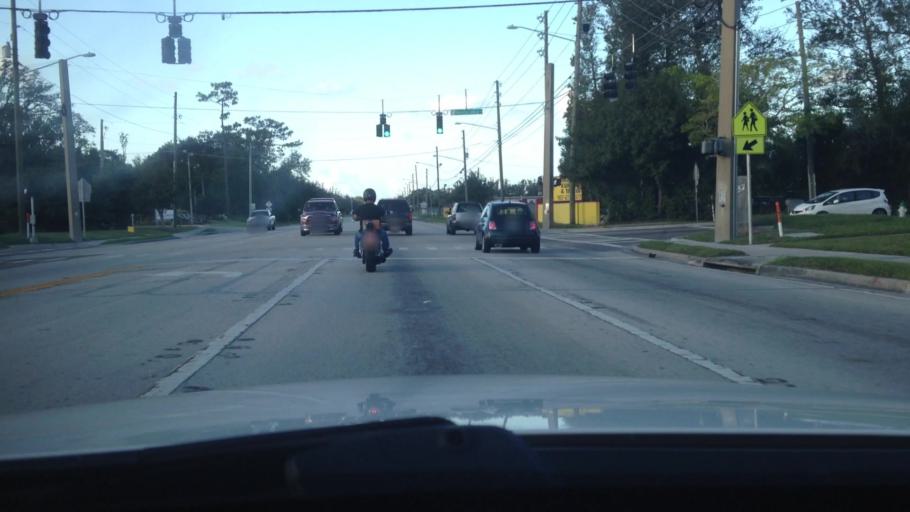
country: US
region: Florida
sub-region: Orange County
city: Union Park
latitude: 28.5533
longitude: -81.2859
